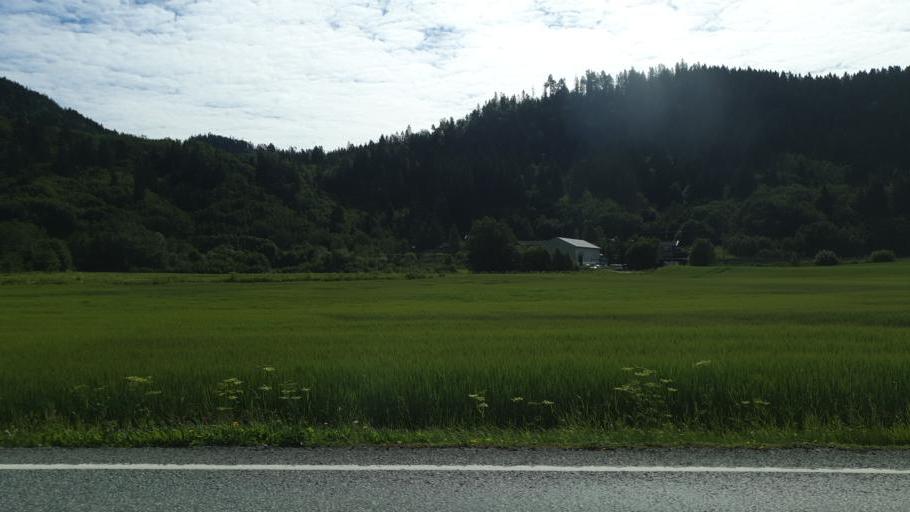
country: NO
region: Sor-Trondelag
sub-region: Melhus
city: Lundamo
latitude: 63.2128
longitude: 10.3056
